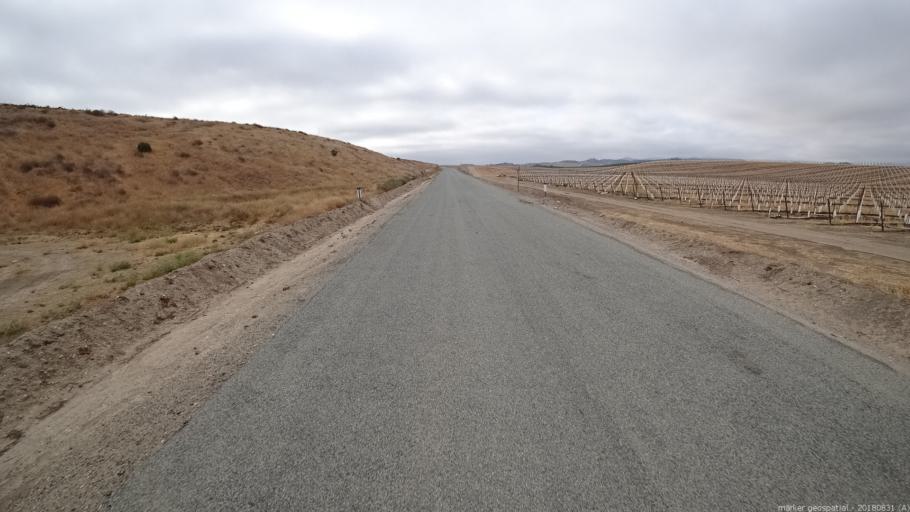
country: US
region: California
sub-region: Monterey County
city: King City
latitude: 36.1627
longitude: -121.1127
